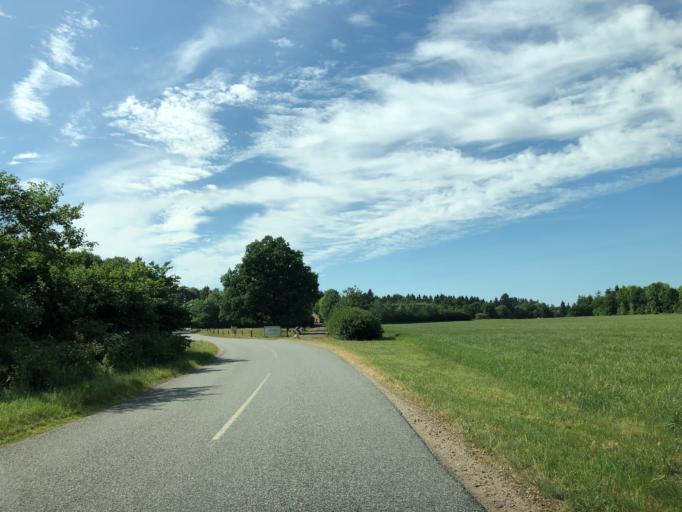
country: DK
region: Central Jutland
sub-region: Herning Kommune
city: Lind
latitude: 56.0180
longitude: 8.9767
